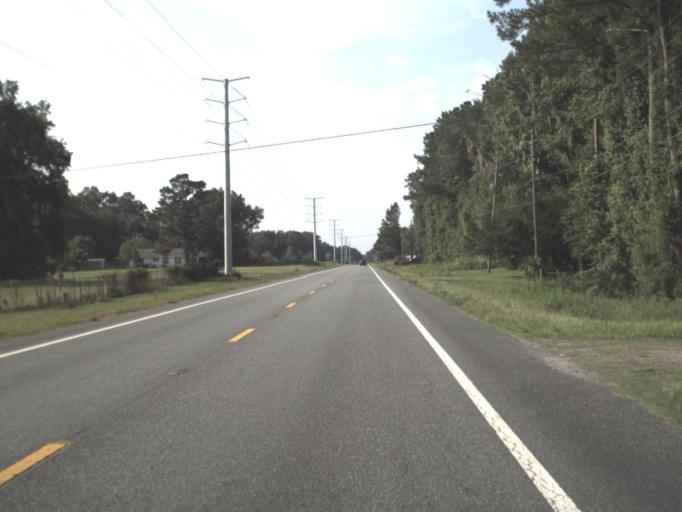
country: US
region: Florida
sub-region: Taylor County
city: Perry
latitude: 30.1562
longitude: -83.5923
